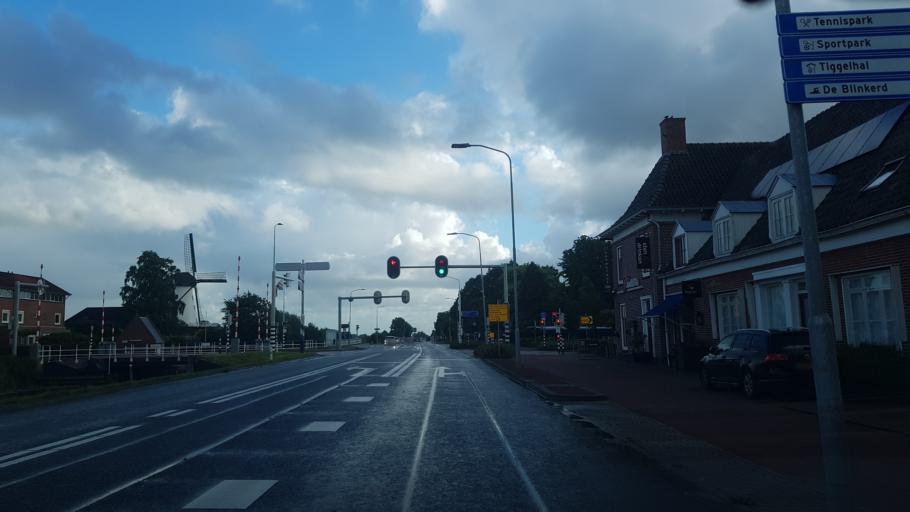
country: NL
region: Groningen
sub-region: Gemeente Bedum
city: Bedum
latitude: 53.2742
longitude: 6.6999
